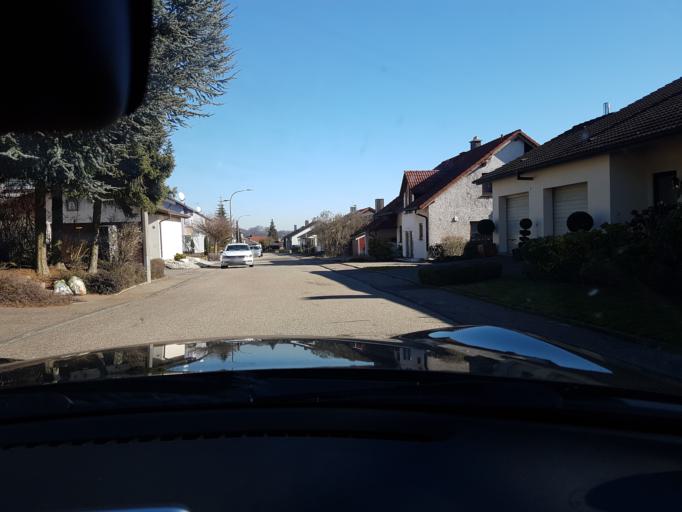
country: DE
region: Baden-Wuerttemberg
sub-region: Karlsruhe Region
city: Osterburken
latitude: 49.4353
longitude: 9.4232
